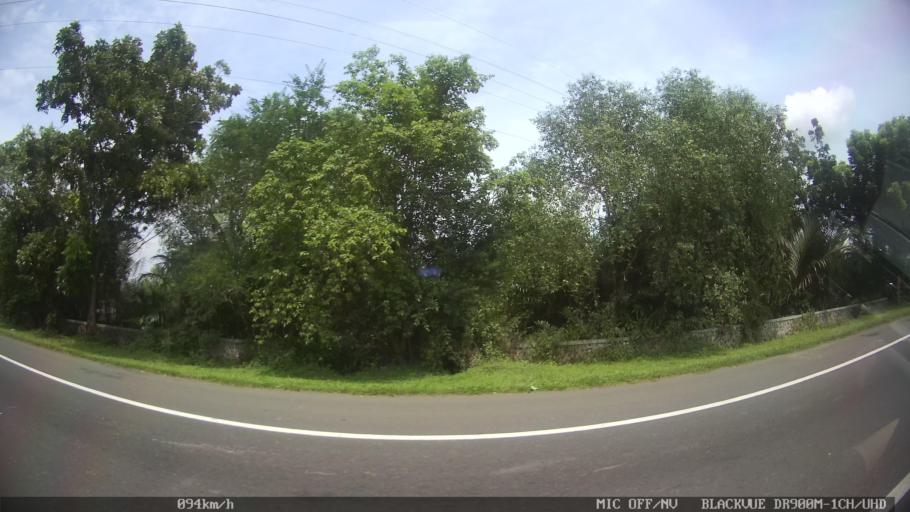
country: ID
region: North Sumatra
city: Labuhan Deli
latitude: 3.7497
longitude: 98.6812
